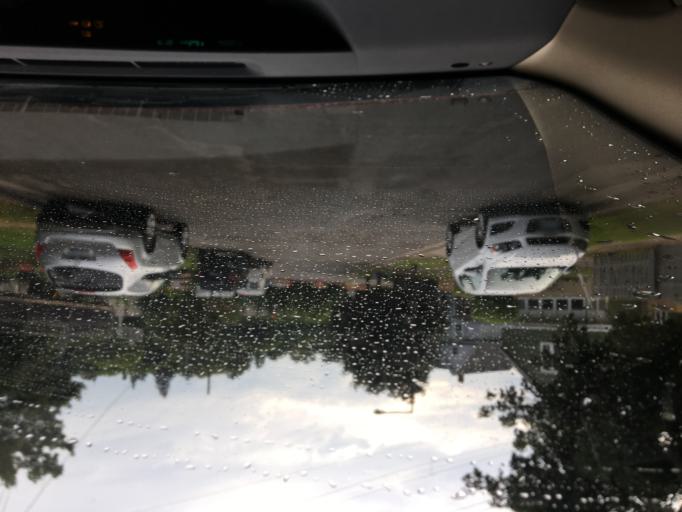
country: US
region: Minnesota
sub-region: Ramsey County
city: Saint Paul
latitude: 44.9526
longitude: -93.0626
